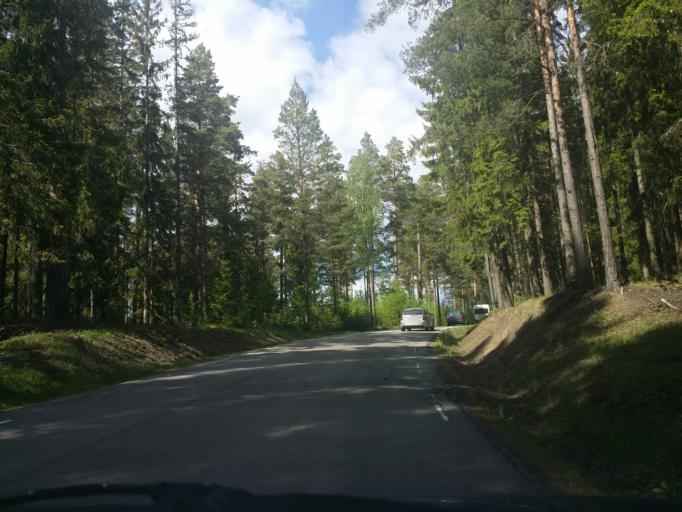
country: NO
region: Oppland
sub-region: Jevnaker
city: Jevnaker
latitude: 60.2303
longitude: 10.3962
